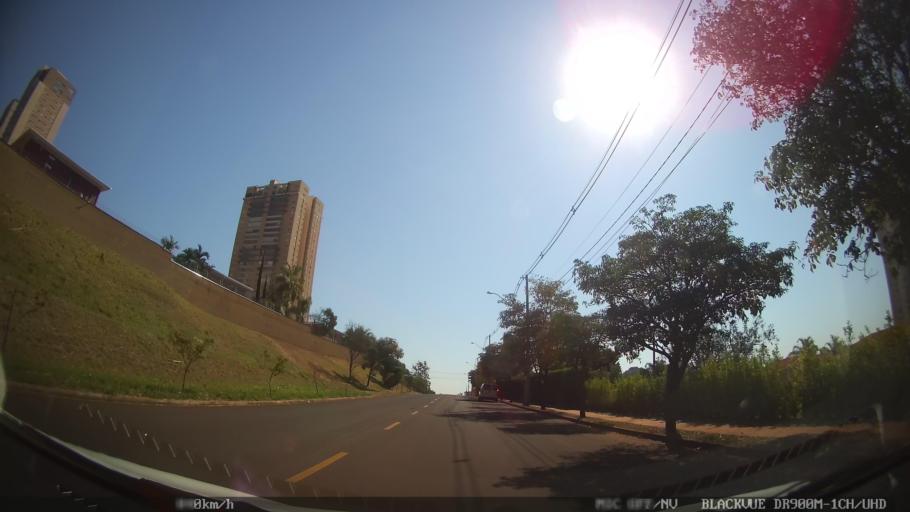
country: BR
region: Sao Paulo
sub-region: Ribeirao Preto
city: Ribeirao Preto
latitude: -21.2178
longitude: -47.8014
